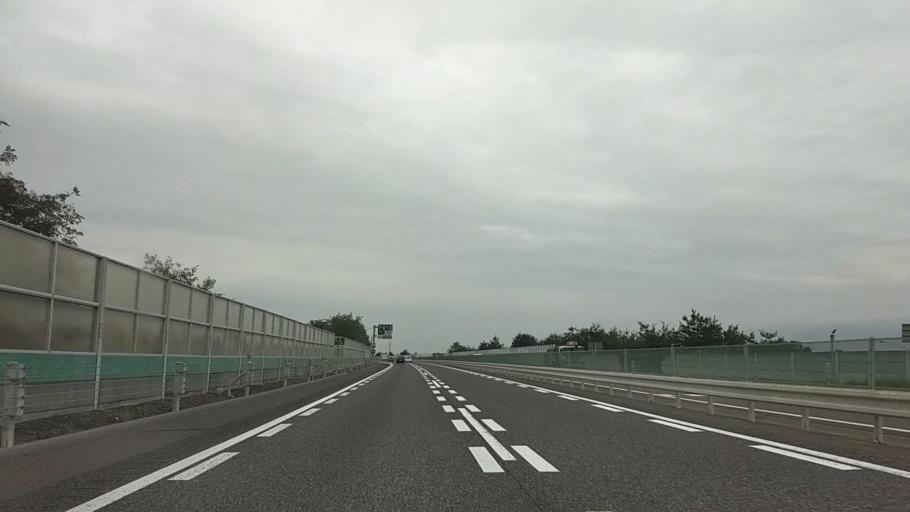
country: JP
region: Nagano
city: Toyoshina
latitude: 36.2759
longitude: 137.9312
